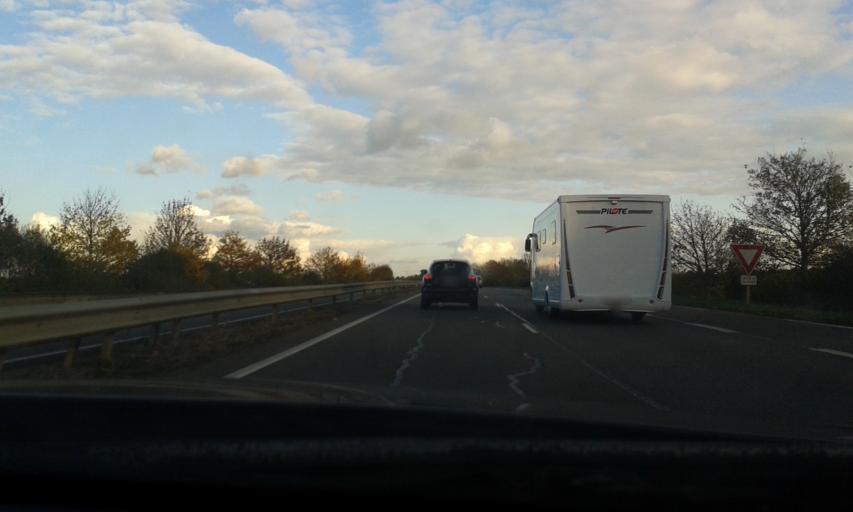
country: FR
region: Centre
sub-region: Departement d'Eure-et-Loir
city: Le Coudray
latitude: 48.4155
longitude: 1.4935
